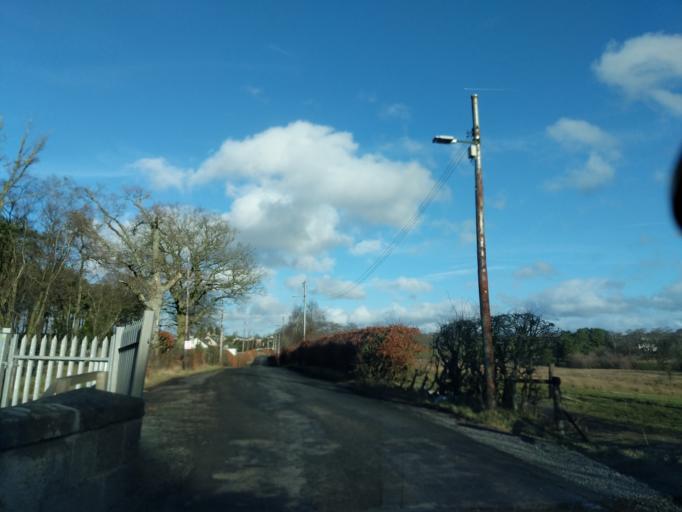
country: GB
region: Scotland
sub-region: South Lanarkshire
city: Carluke
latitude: 55.7210
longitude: -3.8384
